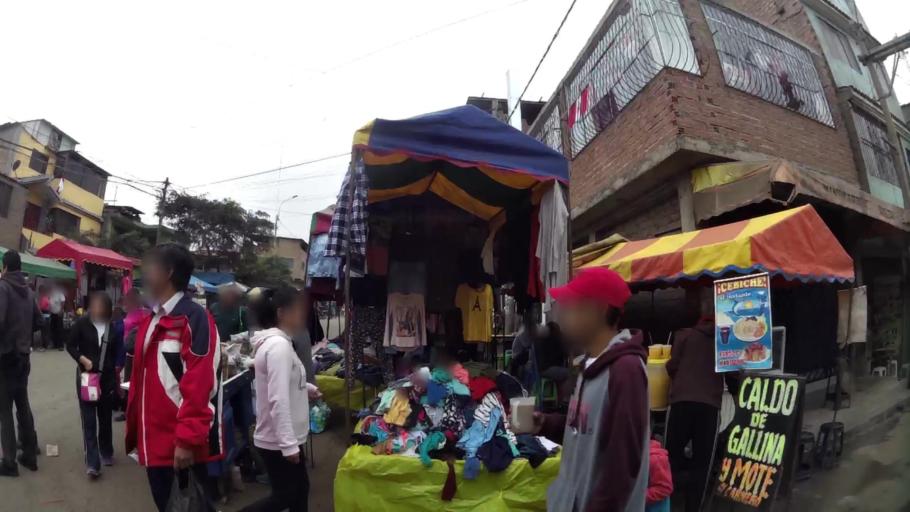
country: PE
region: Lima
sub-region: Lima
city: Surco
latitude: -12.1469
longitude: -76.9690
